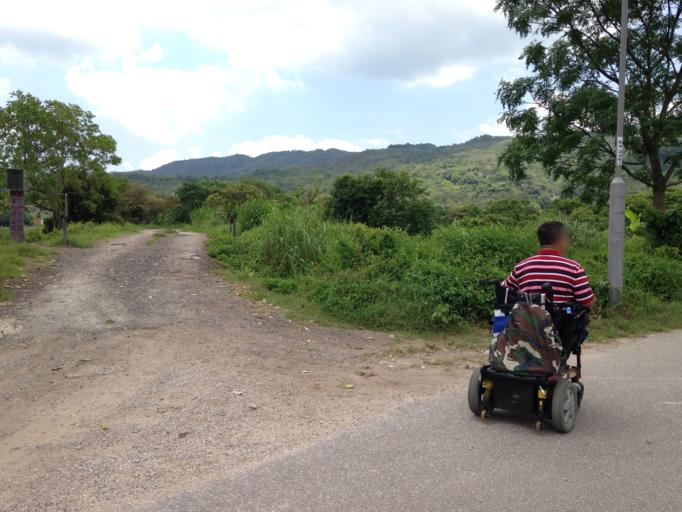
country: CN
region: Guangdong
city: Haishan
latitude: 22.5209
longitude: 114.2079
